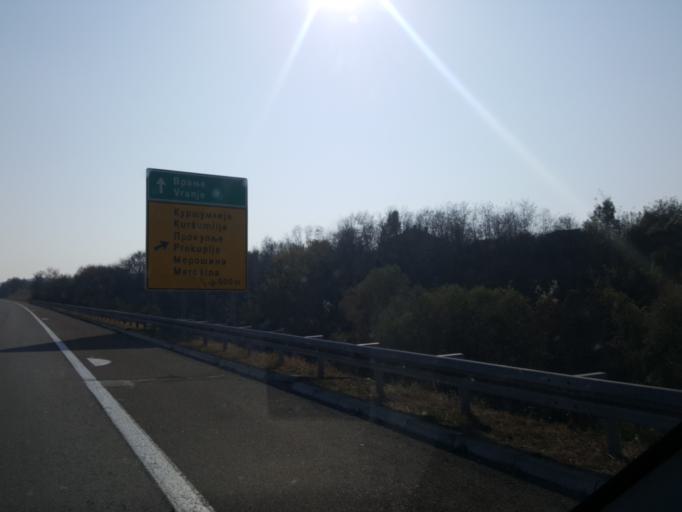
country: RS
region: Central Serbia
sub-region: Nisavski Okrug
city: Merosina
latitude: 43.2881
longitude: 21.7999
